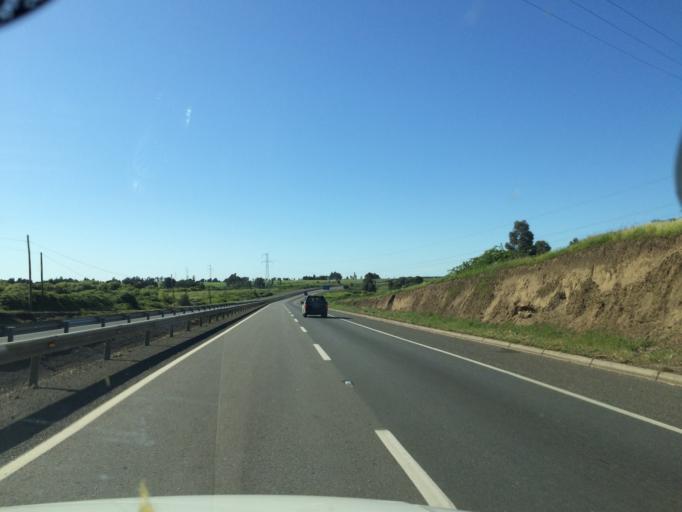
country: CL
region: Biobio
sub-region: Provincia de Biobio
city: Los Angeles
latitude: -37.4644
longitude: -72.4085
